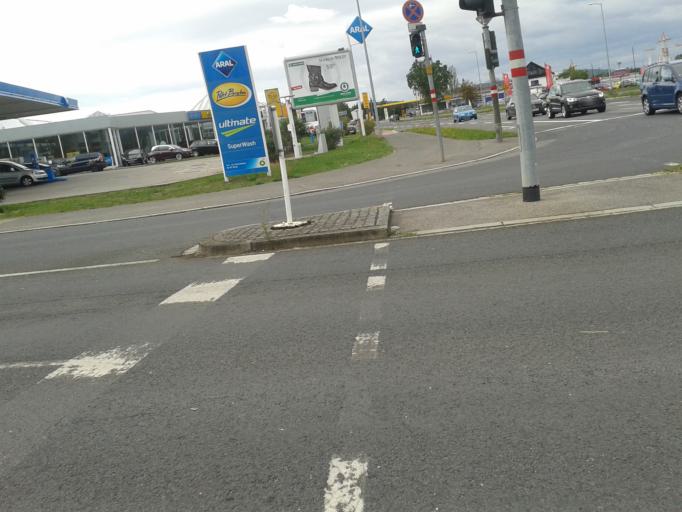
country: DE
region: Bavaria
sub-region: Upper Franconia
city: Bamberg
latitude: 49.9140
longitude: 10.9093
